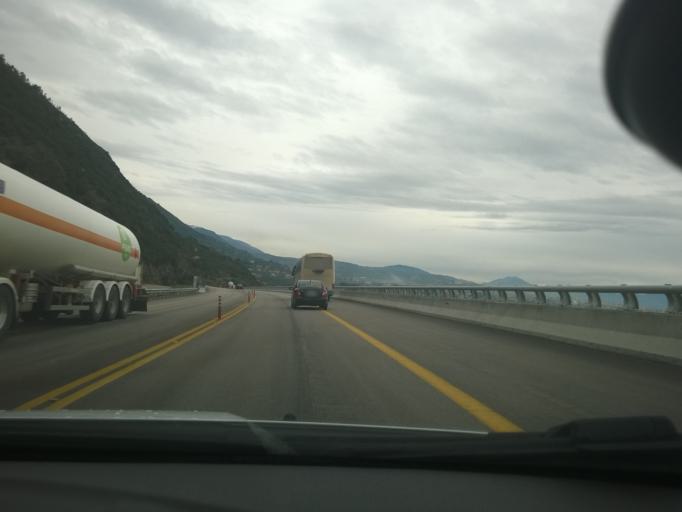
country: GR
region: West Greece
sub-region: Nomos Achaias
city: Temeni
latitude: 38.2135
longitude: 22.1212
